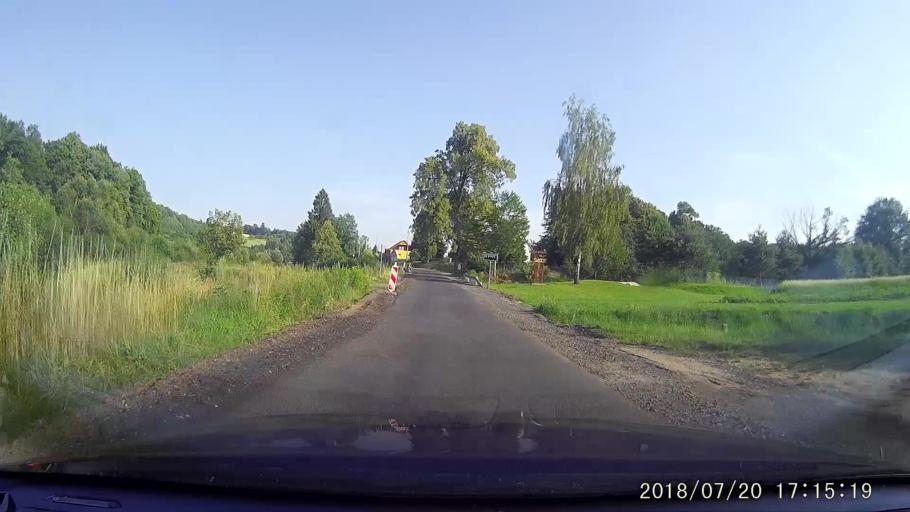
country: PL
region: Lower Silesian Voivodeship
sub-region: Powiat lubanski
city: Lesna
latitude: 51.0057
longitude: 15.2778
